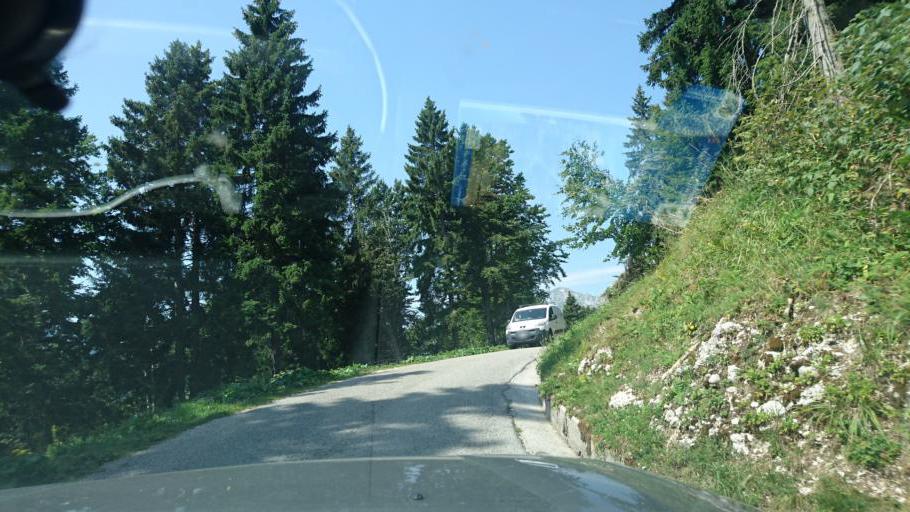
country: IT
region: Friuli Venezia Giulia
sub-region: Provincia di Udine
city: Malborghetto
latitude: 46.3992
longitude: 13.4602
